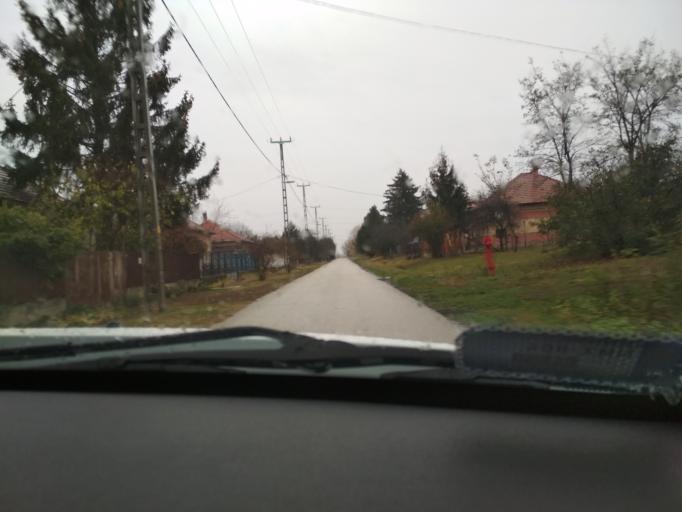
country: HU
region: Csongrad
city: Opusztaszer
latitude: 46.4376
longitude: 20.1309
